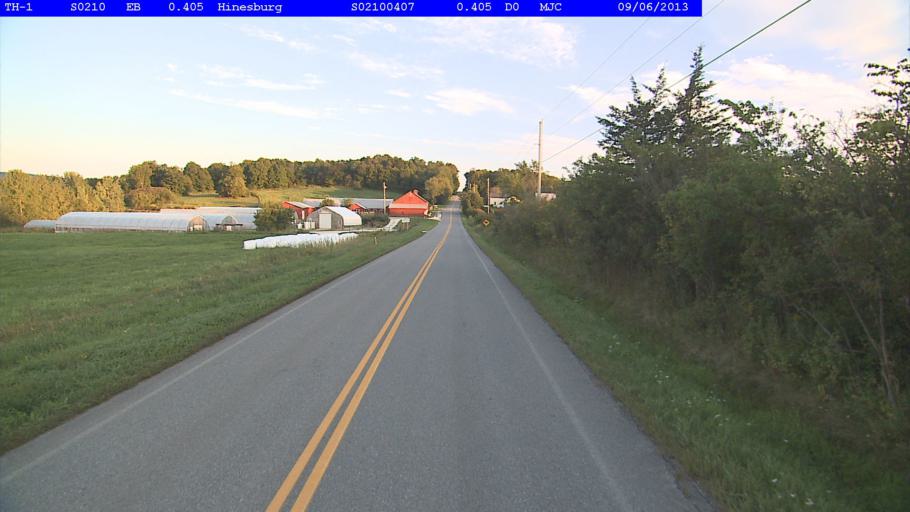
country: US
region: Vermont
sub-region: Chittenden County
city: Hinesburg
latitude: 44.3579
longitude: -73.1571
